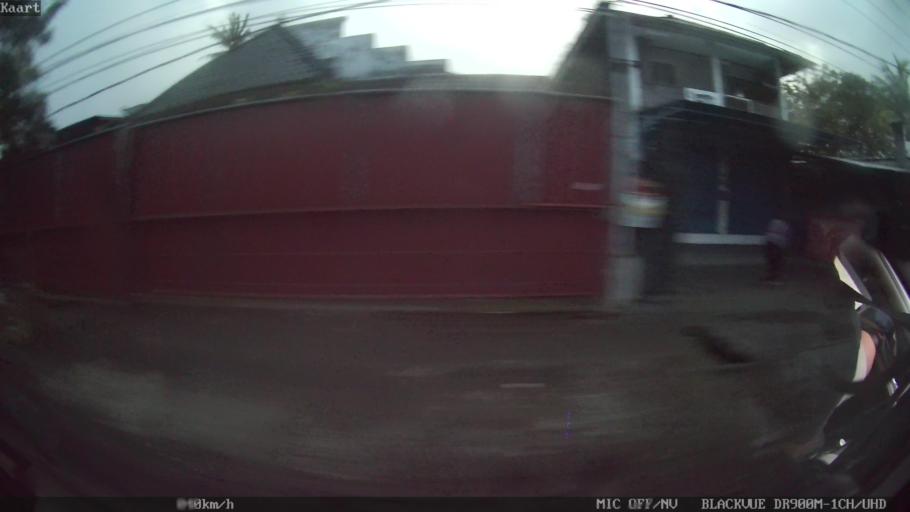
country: ID
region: Bali
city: Banjar Batur
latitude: -8.5940
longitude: 115.2152
